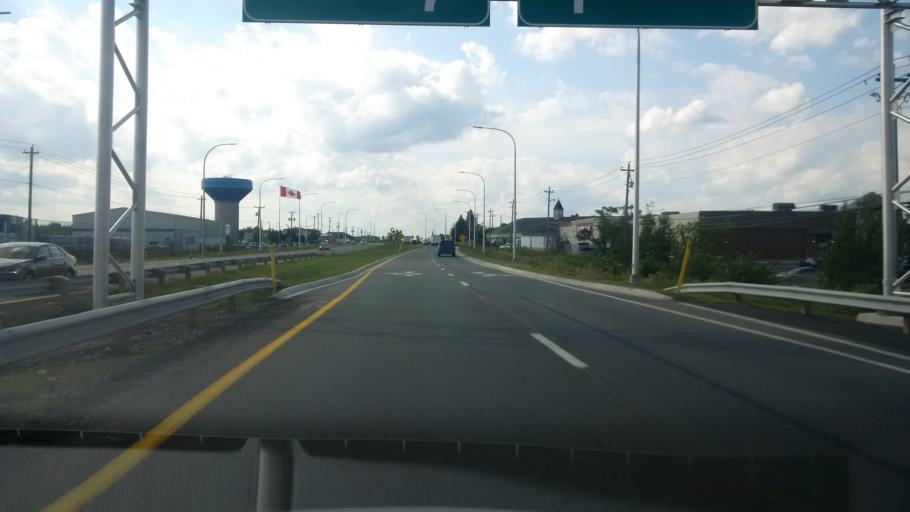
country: CA
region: New Brunswick
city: Fredericton
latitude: 45.9398
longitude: -66.6671
